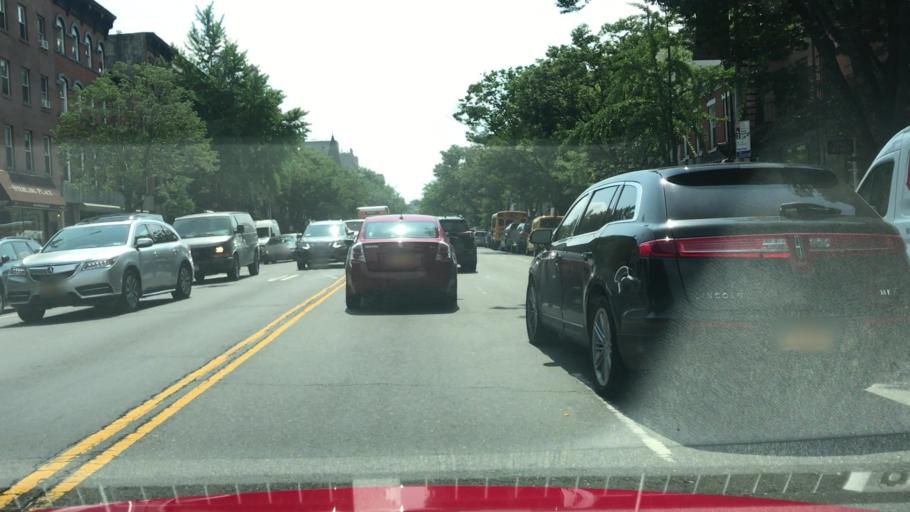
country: US
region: New York
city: New York City
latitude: 40.6876
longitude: -73.9867
